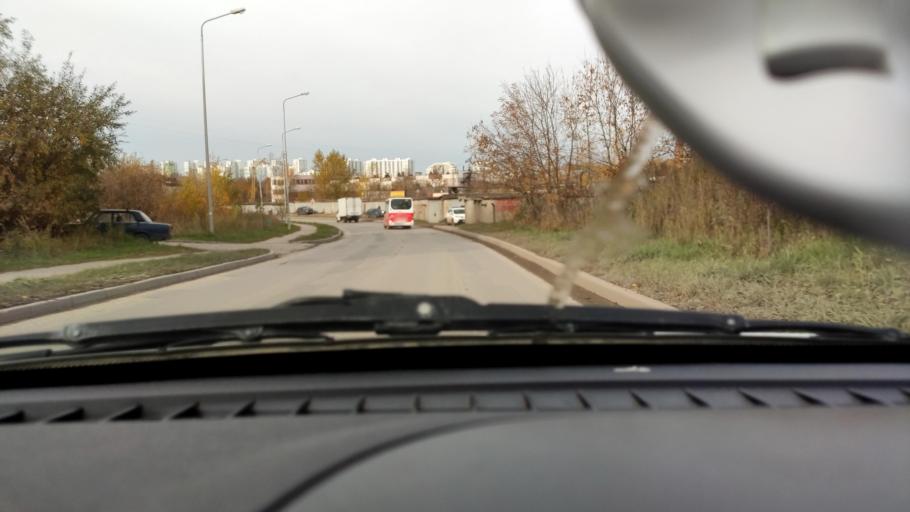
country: RU
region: Perm
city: Perm
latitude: 57.9789
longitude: 56.2828
